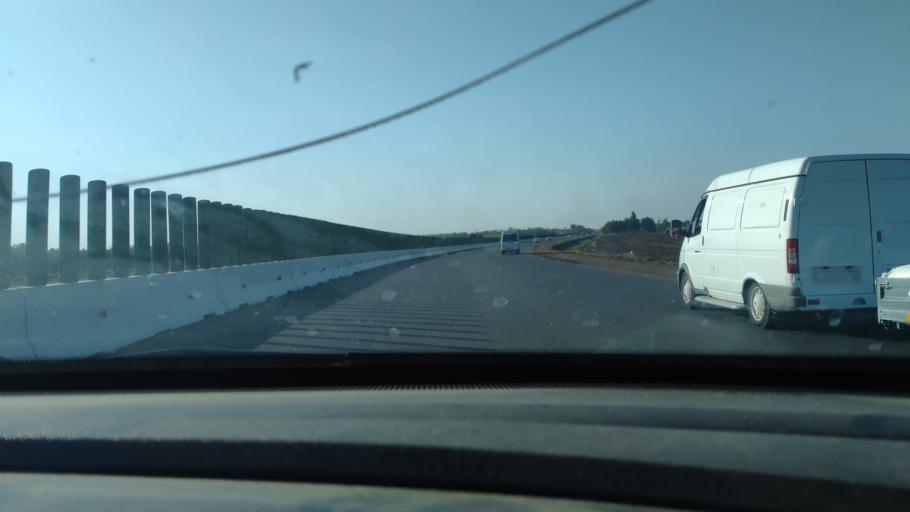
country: RU
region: Krasnodarskiy
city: Medvedovskaya
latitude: 45.4699
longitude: 38.9765
